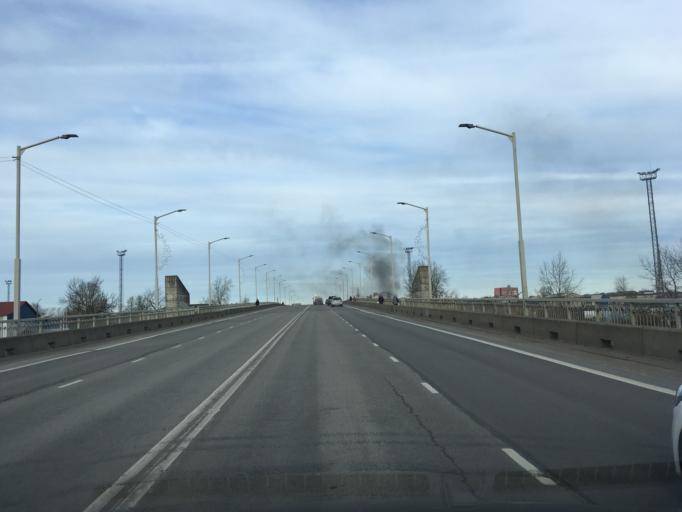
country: EE
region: Ida-Virumaa
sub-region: Narva linn
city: Narva
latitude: 59.3702
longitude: 28.1848
